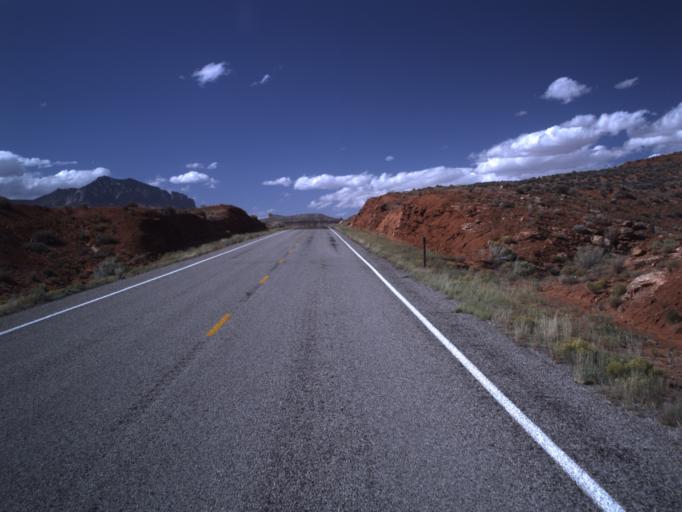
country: US
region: Utah
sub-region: Wayne County
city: Loa
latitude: 38.0635
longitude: -110.5998
